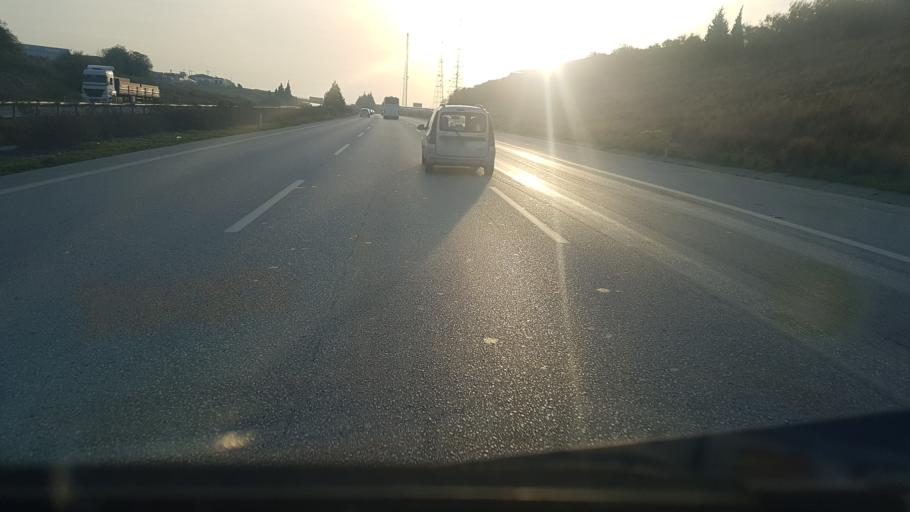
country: TR
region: Adana
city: Yakapinar
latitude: 36.9890
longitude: 35.6021
